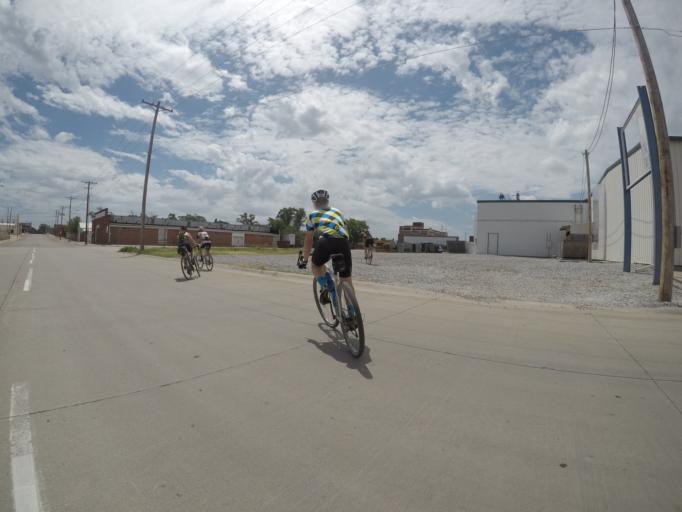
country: US
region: Nebraska
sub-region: Gage County
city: Beatrice
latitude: 40.2648
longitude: -96.7514
